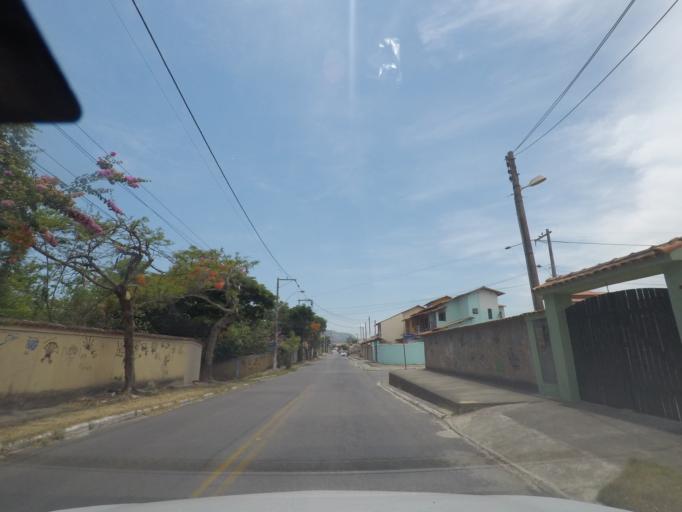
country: BR
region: Rio de Janeiro
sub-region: Marica
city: Marica
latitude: -22.9671
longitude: -42.9591
